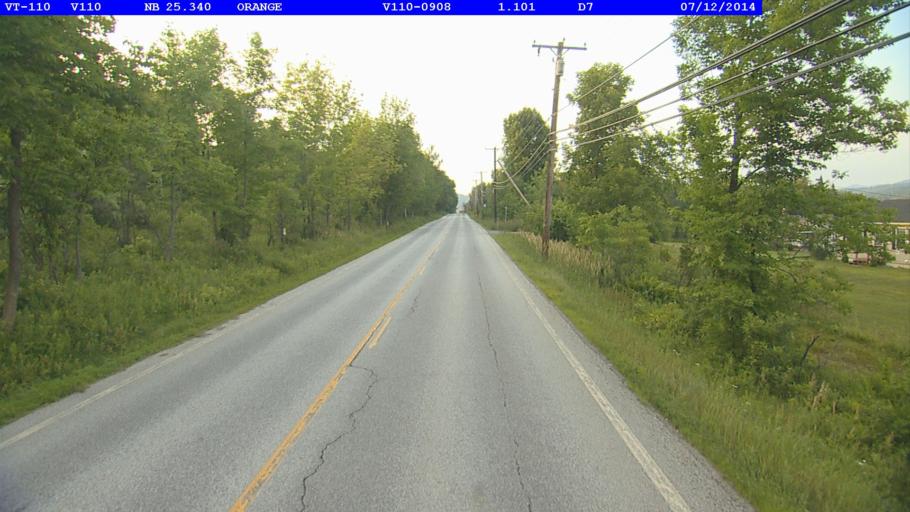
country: US
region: Vermont
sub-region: Washington County
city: South Barre
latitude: 44.1399
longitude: -72.4331
